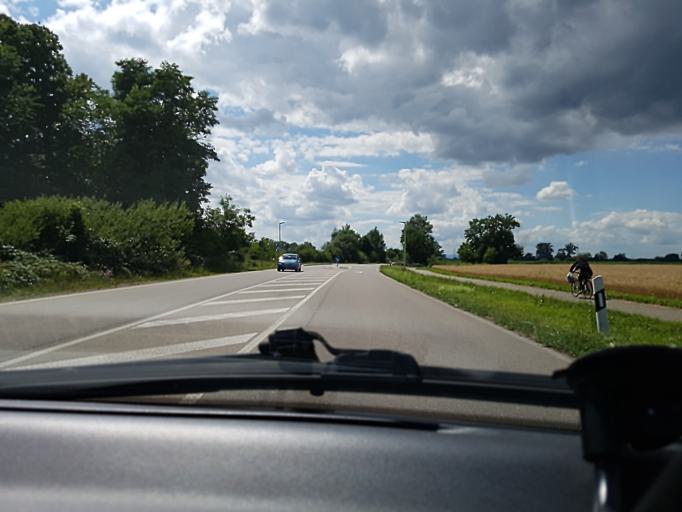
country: DE
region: Baden-Wuerttemberg
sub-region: Freiburg Region
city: Willstatt
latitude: 48.5336
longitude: 7.8795
